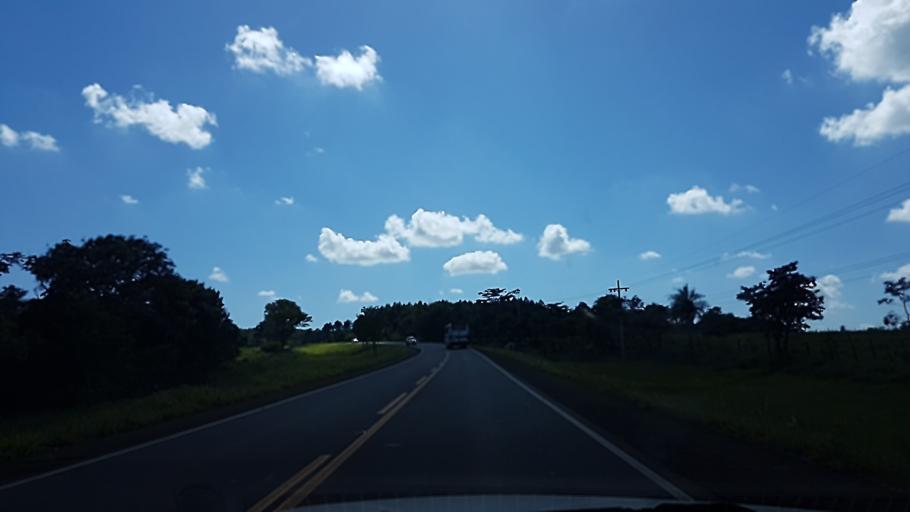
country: PY
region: Itapua
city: Carmen del Parana
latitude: -27.2205
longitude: -56.1026
